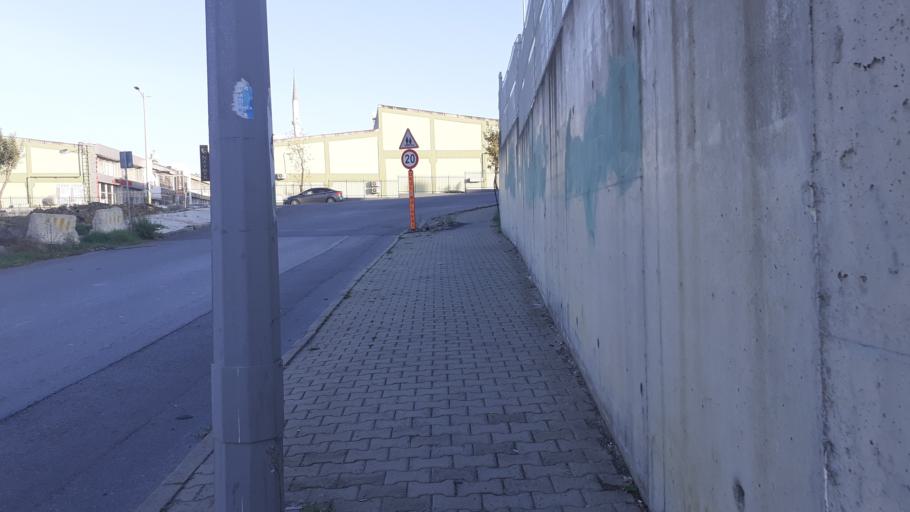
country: TR
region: Istanbul
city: Basaksehir
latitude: 41.0687
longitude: 28.7829
